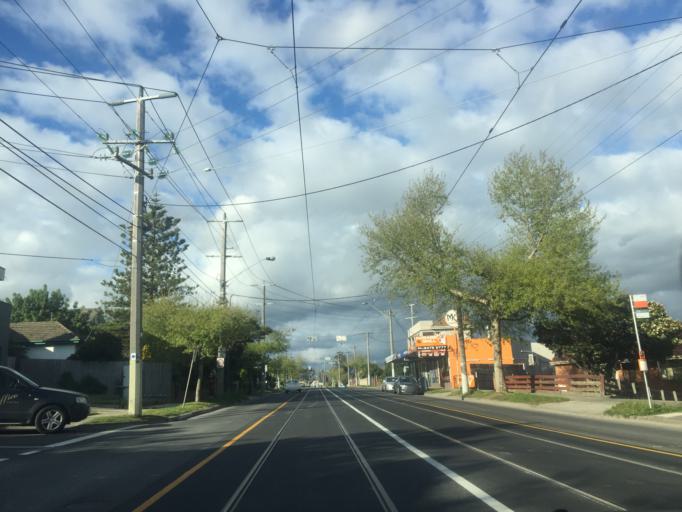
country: AU
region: Victoria
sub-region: Darebin
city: Kingsbury
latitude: -37.7277
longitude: 145.0195
